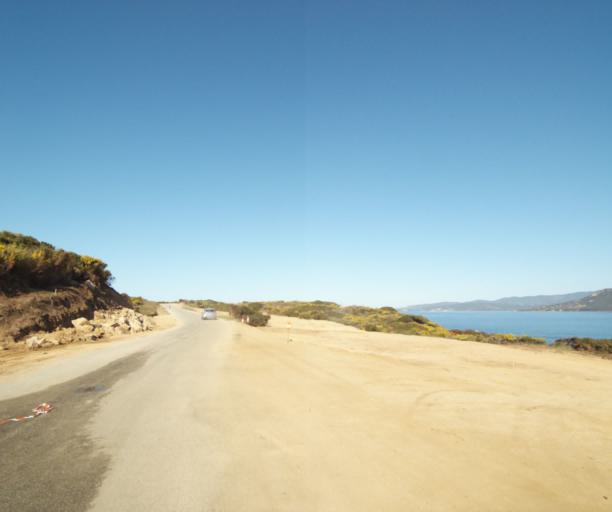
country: FR
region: Corsica
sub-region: Departement de la Corse-du-Sud
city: Propriano
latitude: 41.6707
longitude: 8.8860
